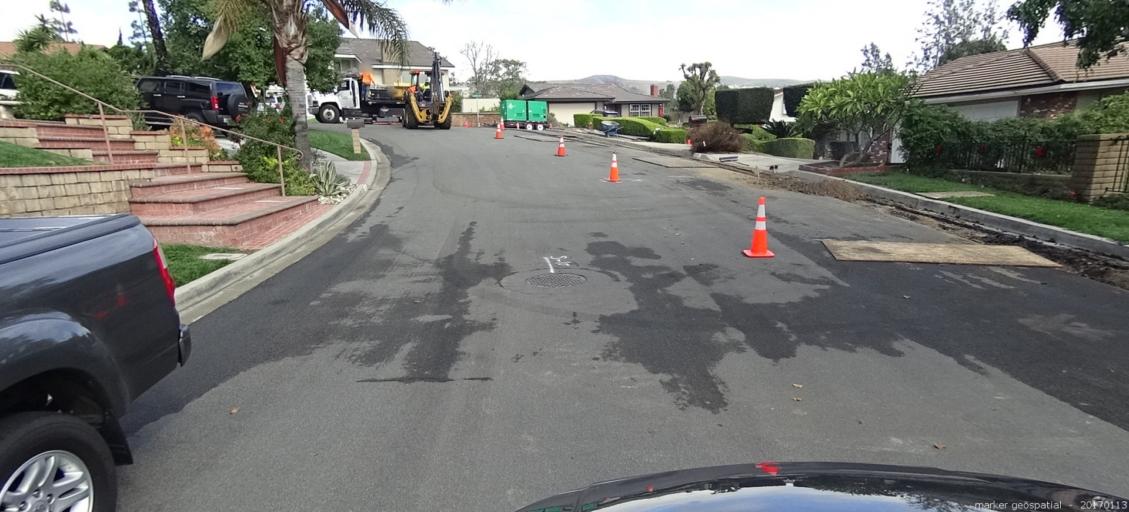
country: US
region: California
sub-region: Orange County
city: Yorba Linda
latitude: 33.8877
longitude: -117.7992
